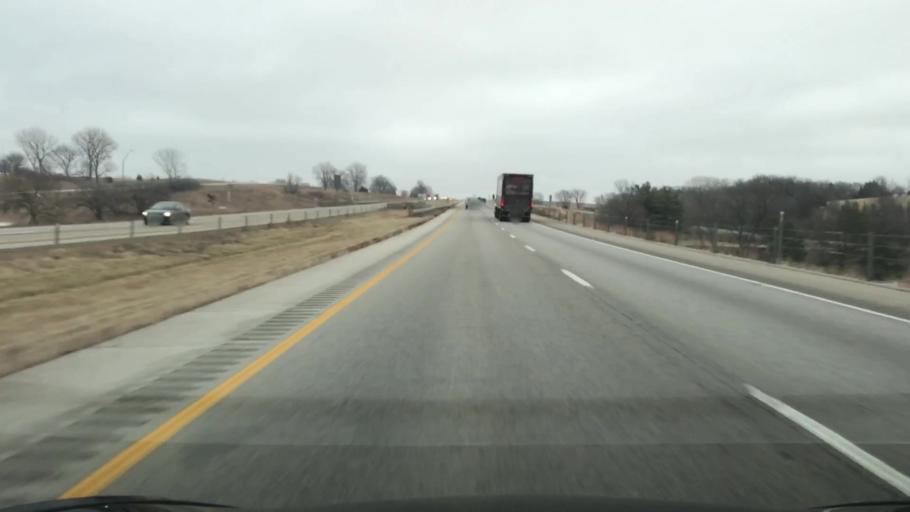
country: US
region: Iowa
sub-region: Madison County
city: Earlham
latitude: 41.5175
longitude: -94.1253
